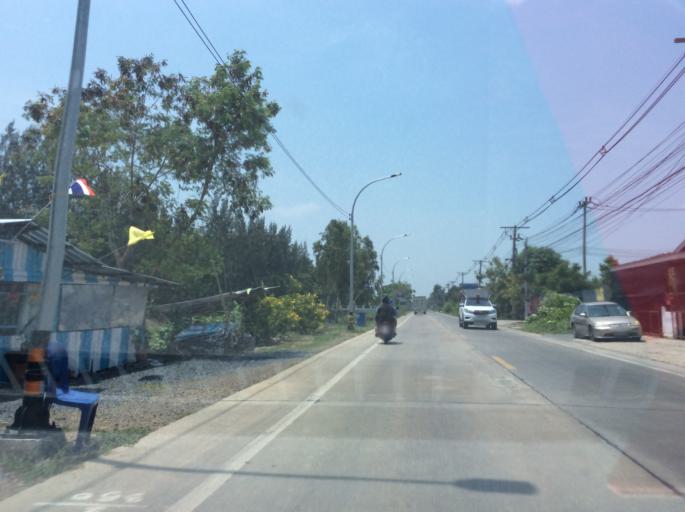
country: TH
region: Pathum Thani
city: Ban Rangsit
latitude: 14.0256
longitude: 100.7786
